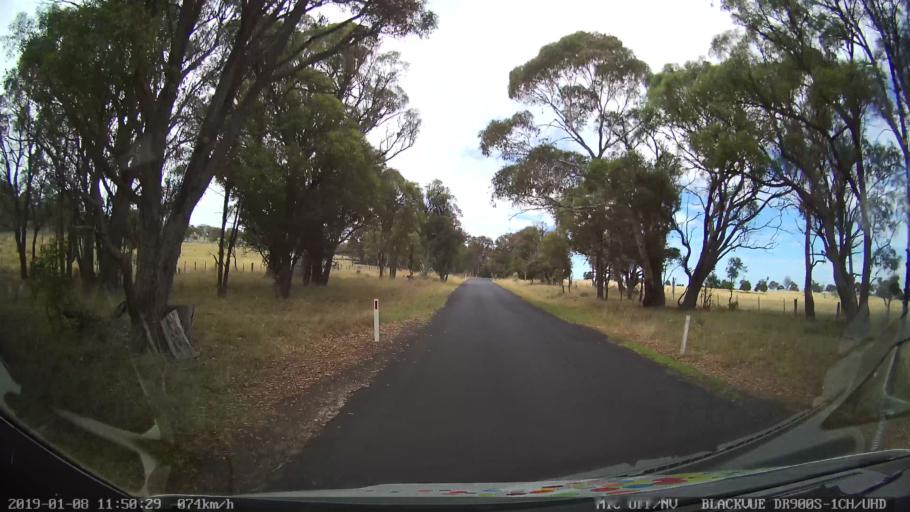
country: AU
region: New South Wales
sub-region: Armidale Dumaresq
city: Armidale
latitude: -30.3832
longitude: 151.5574
